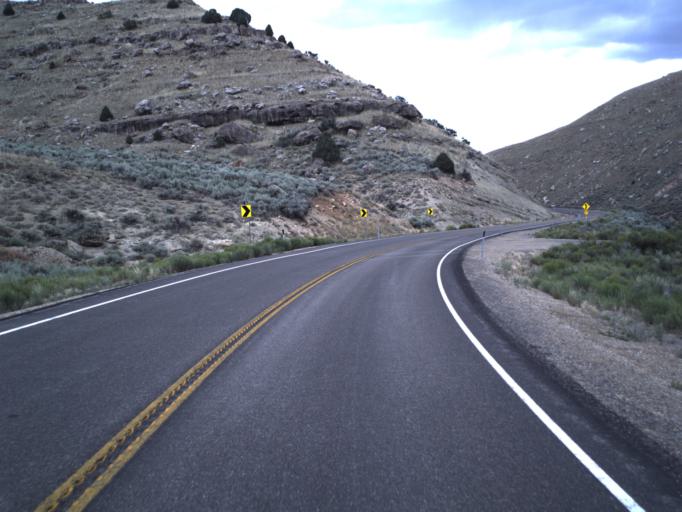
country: US
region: Utah
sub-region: Carbon County
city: Helper
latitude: 39.7830
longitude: -110.7933
